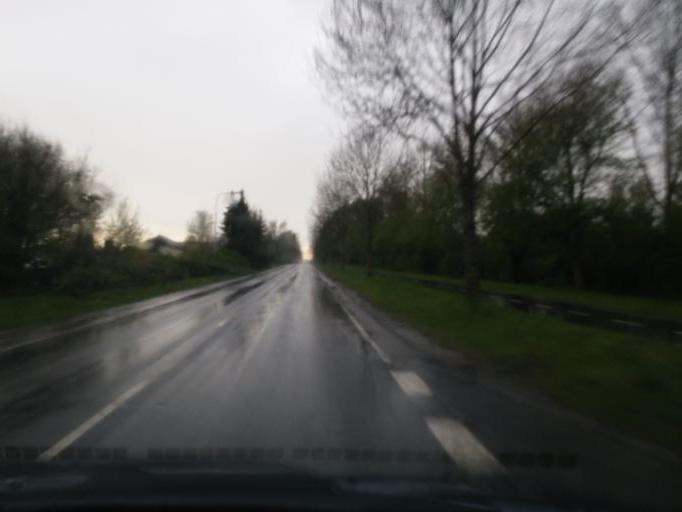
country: DK
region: South Denmark
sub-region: Odense Kommune
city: Bellinge
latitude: 55.3406
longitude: 10.2984
